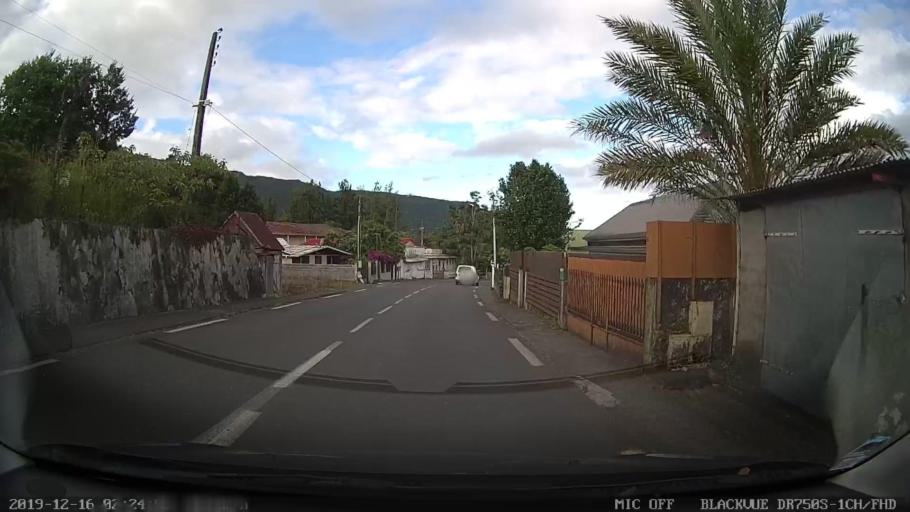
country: RE
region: Reunion
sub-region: Reunion
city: Saint-Benoit
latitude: -21.1393
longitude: 55.6231
